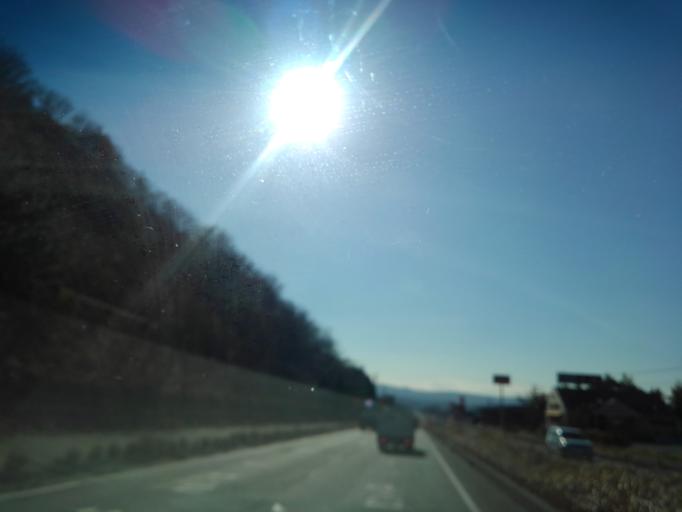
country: JP
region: Chiba
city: Kimitsu
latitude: 35.3372
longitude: 139.9220
